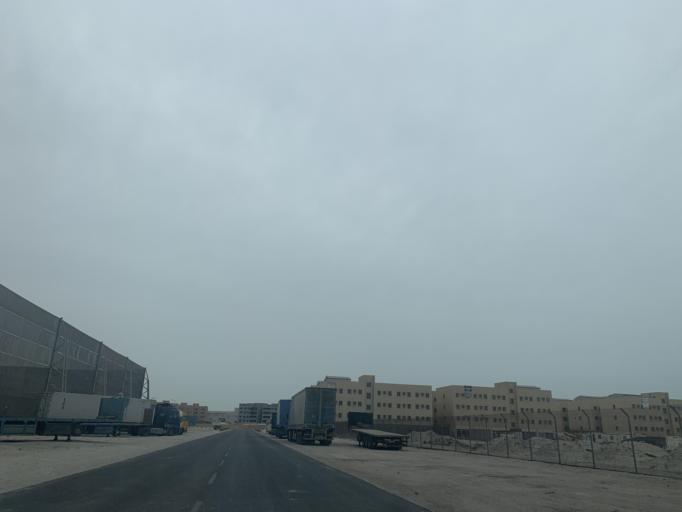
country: BH
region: Muharraq
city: Al Hadd
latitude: 26.2064
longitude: 50.6804
